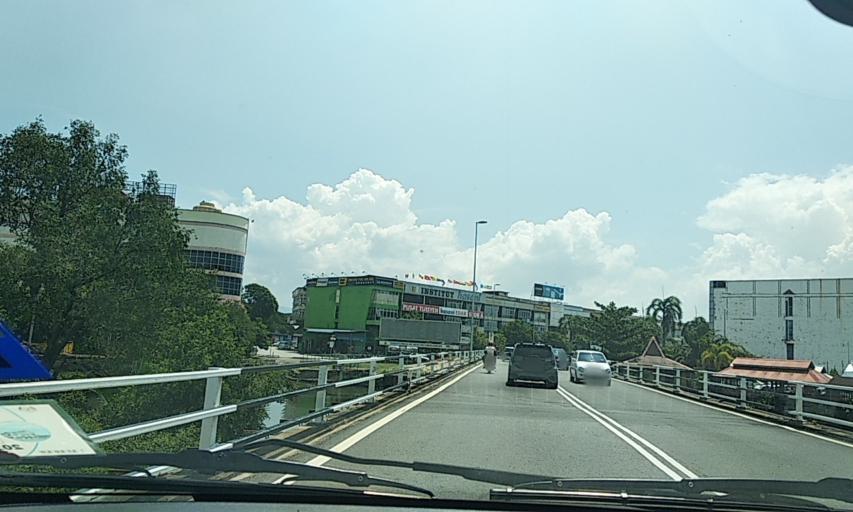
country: MY
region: Kedah
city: Sungai Petani
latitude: 5.6383
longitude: 100.4824
